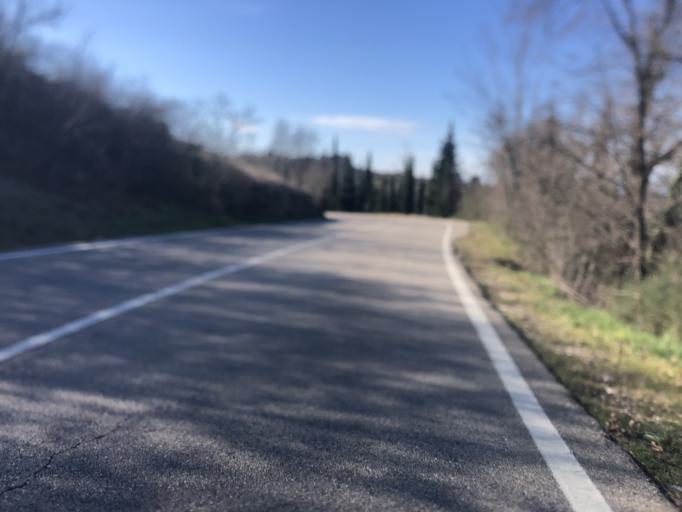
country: IT
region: Veneto
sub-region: Provincia di Verona
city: Volargne
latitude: 45.5368
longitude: 10.8326
